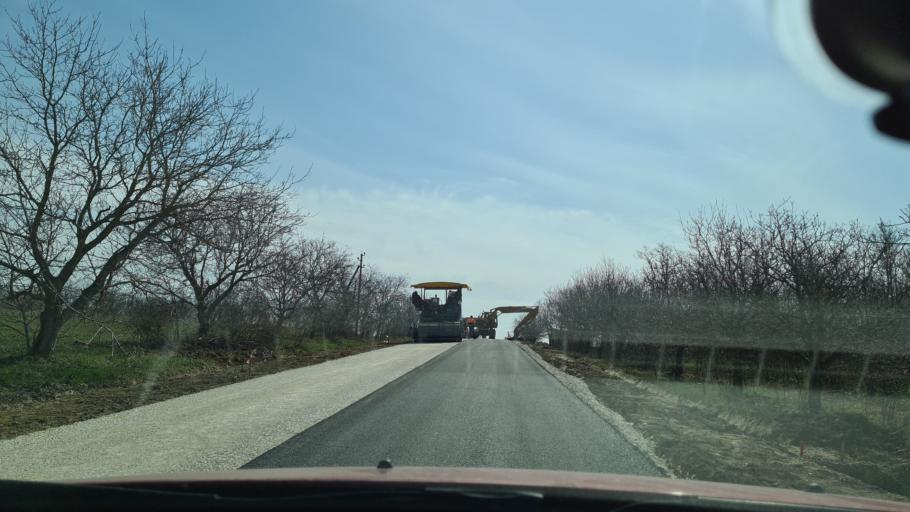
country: MD
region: Ungheni
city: Ungheni
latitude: 47.2635
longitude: 27.9662
